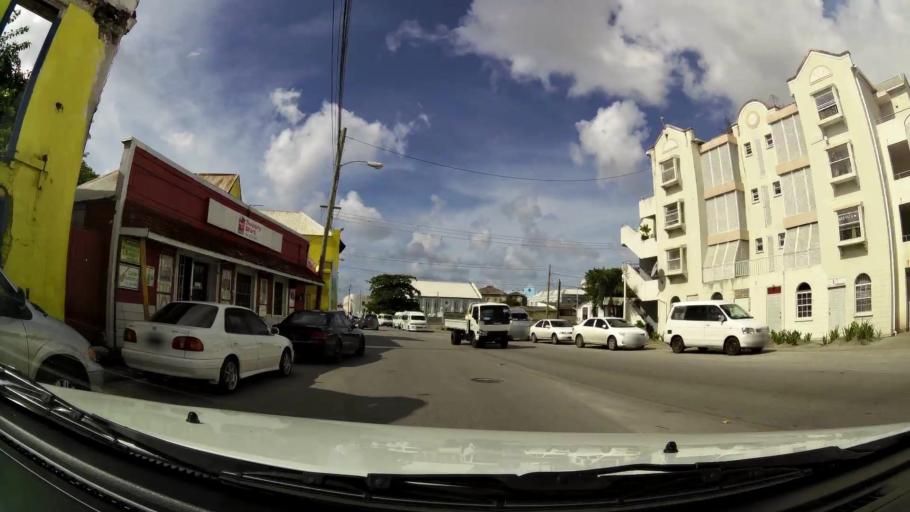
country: BB
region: Saint Michael
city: Bridgetown
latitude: 13.0931
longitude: -59.6121
